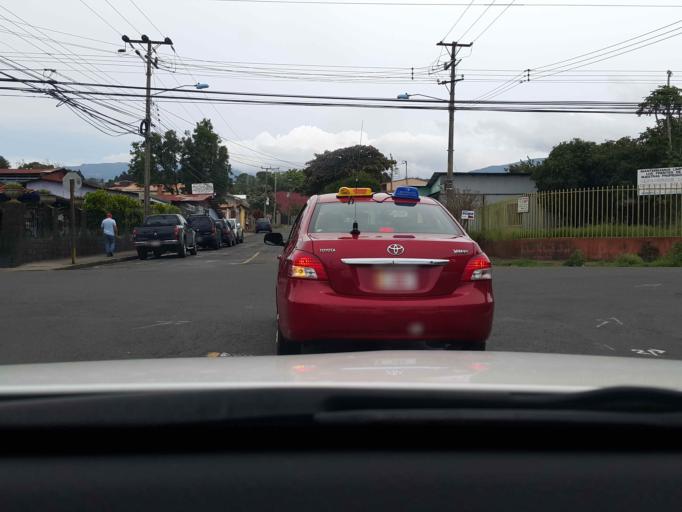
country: CR
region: Heredia
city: San Josecito
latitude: 10.0157
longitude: -84.0965
